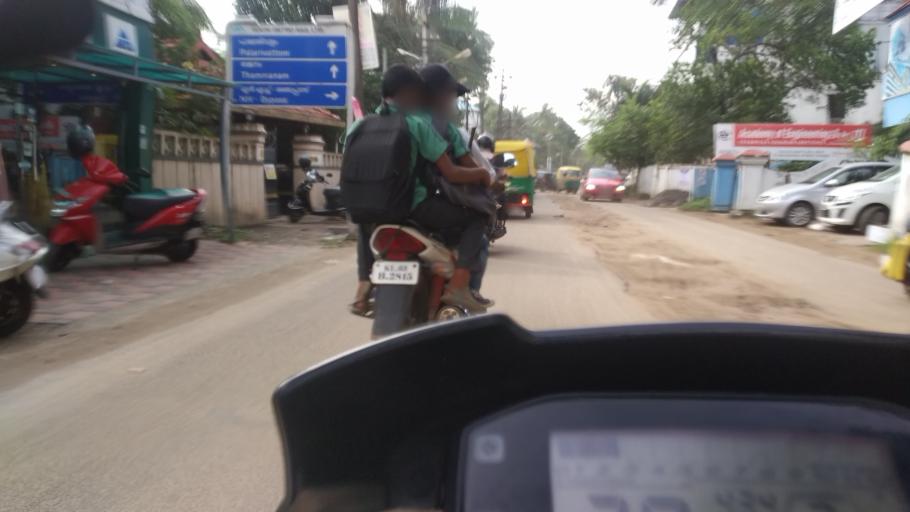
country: IN
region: Kerala
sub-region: Ernakulam
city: Cochin
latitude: 9.9797
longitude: 76.3138
